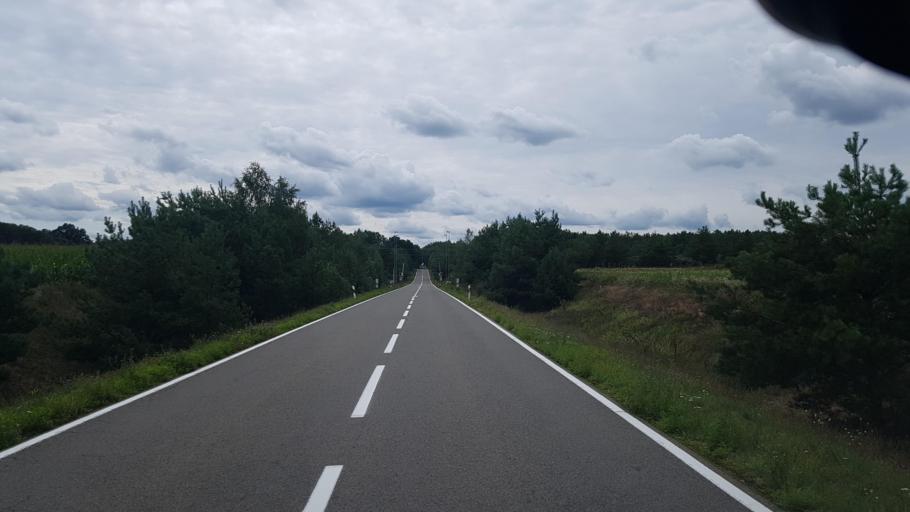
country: DE
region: Brandenburg
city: Spremberg
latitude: 51.6099
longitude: 14.3421
